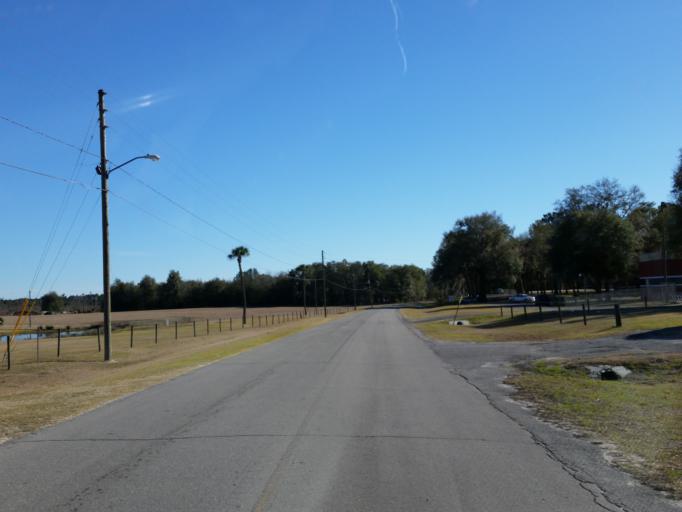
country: US
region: Florida
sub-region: Hamilton County
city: Jasper
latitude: 30.5098
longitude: -82.9529
